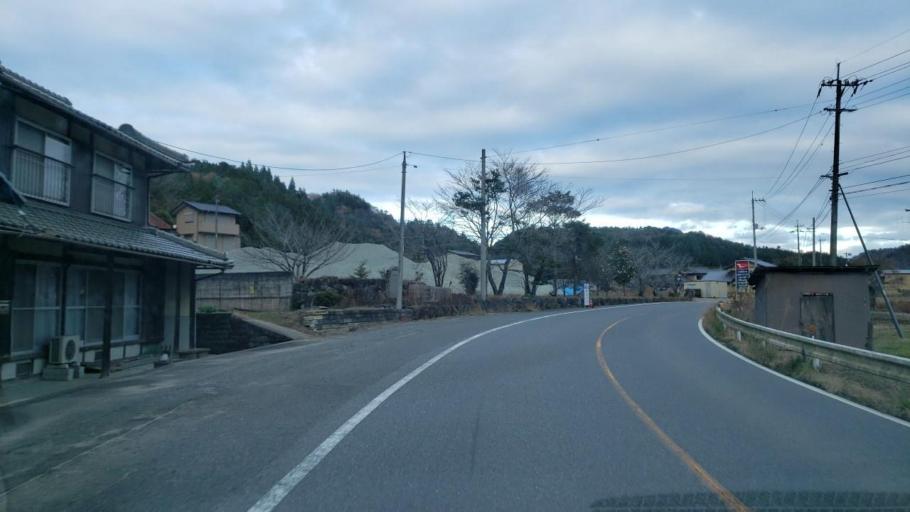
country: JP
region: Tokushima
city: Wakimachi
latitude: 34.1681
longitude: 134.1532
